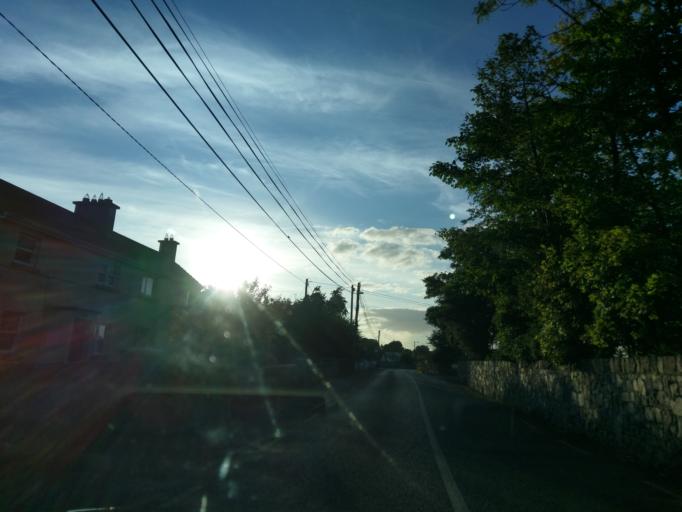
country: IE
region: Connaught
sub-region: County Galway
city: Athenry
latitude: 53.3006
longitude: -8.7633
